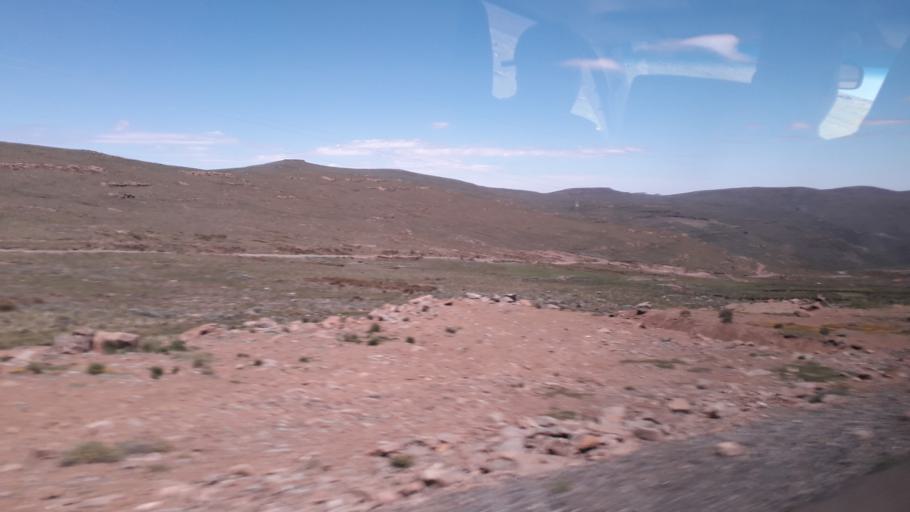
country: ZA
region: Orange Free State
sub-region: Thabo Mofutsanyana District Municipality
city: Phuthaditjhaba
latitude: -28.8149
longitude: 28.7178
